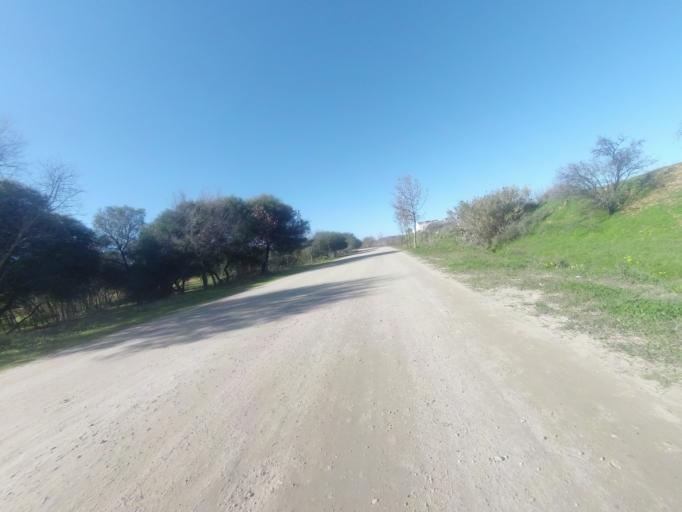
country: ES
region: Andalusia
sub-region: Provincia de Huelva
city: Palos de la Frontera
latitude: 37.2337
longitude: -6.8937
